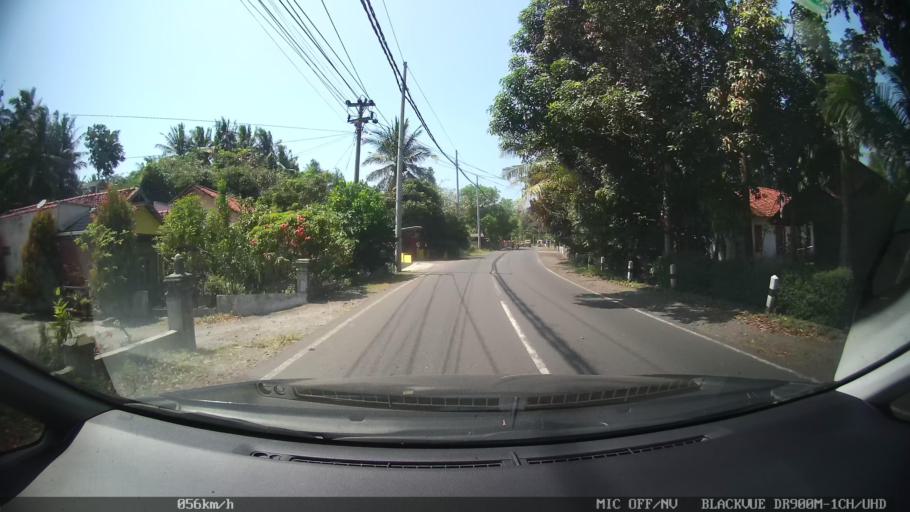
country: ID
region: Daerah Istimewa Yogyakarta
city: Srandakan
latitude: -7.9022
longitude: 110.0723
